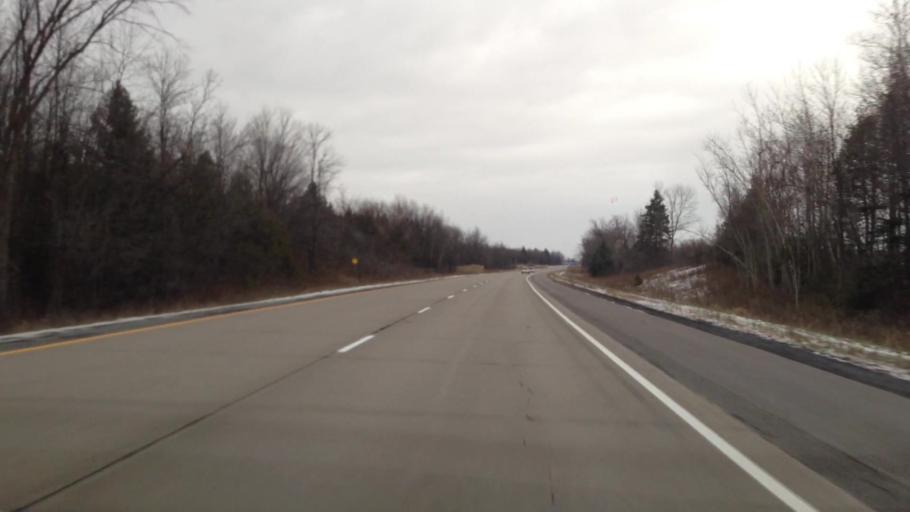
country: CA
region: Ontario
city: Hawkesbury
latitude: 45.5028
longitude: -74.5931
